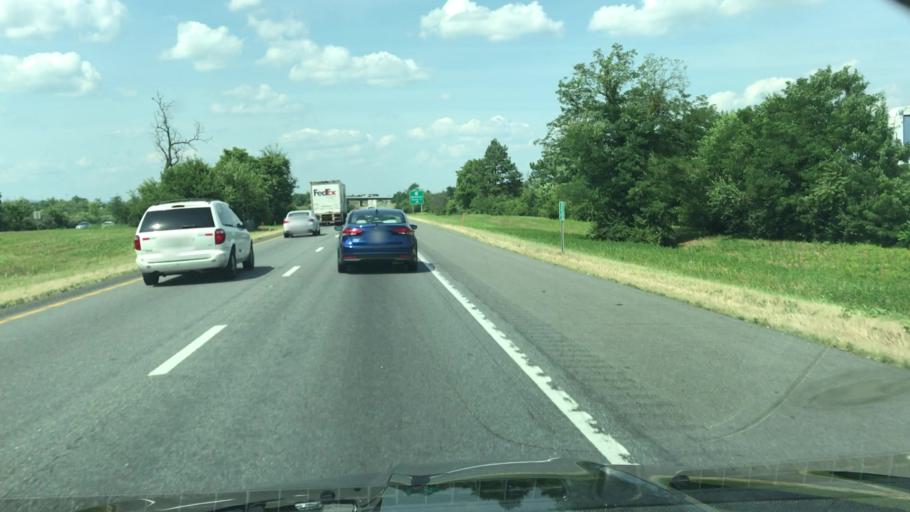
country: US
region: West Virginia
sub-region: Berkeley County
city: Inwood
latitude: 39.2832
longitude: -78.0879
